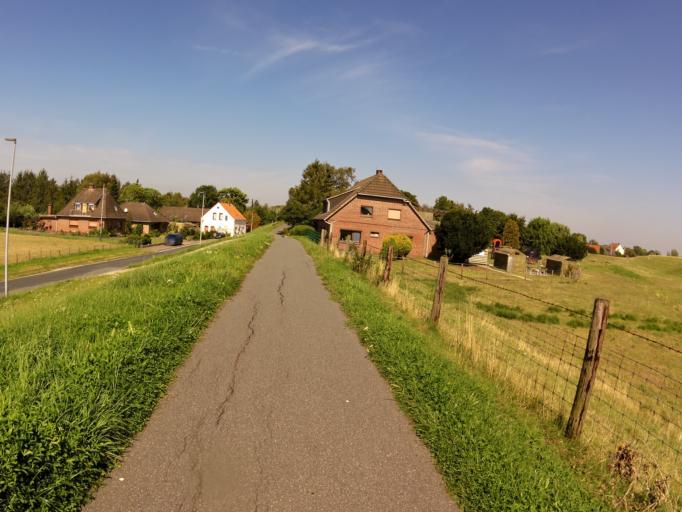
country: DE
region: Lower Saxony
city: Brake (Unterweser)
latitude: 53.2878
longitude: 8.4813
